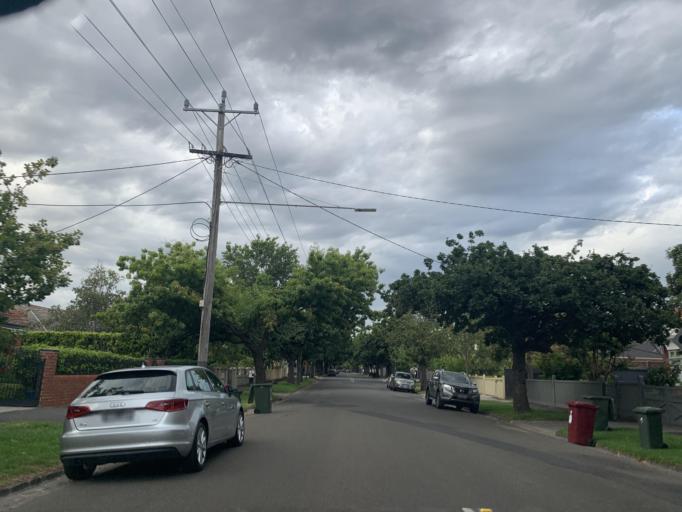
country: AU
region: Victoria
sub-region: Stonnington
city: Malvern East
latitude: -37.8694
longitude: 145.0437
